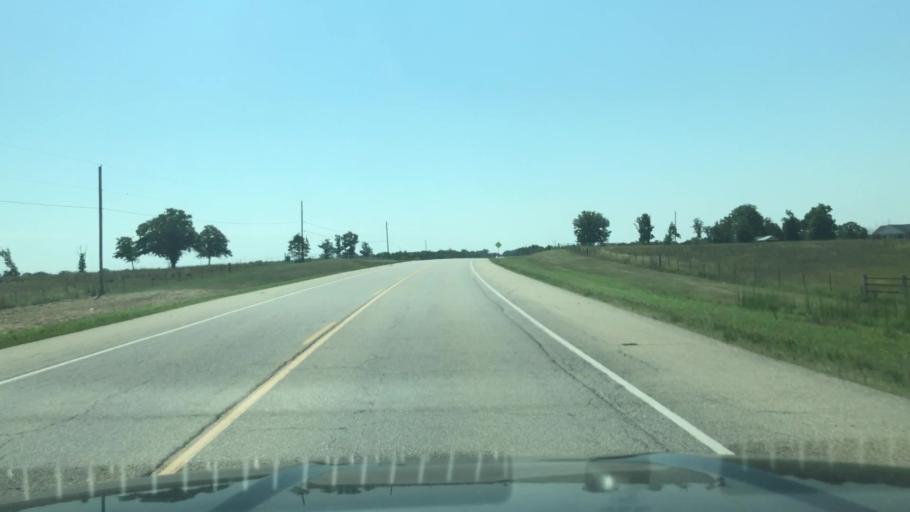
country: US
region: Oklahoma
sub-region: Creek County
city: Mannford
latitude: 35.9981
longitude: -96.3629
